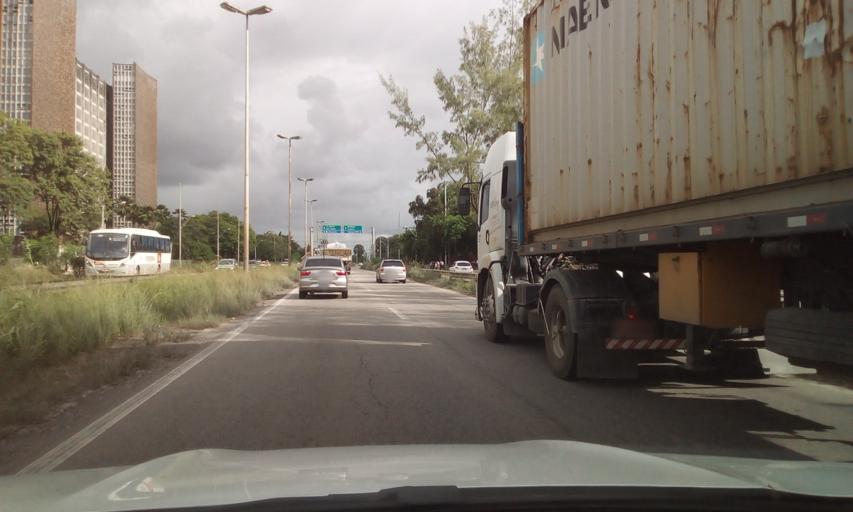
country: BR
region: Pernambuco
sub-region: Recife
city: Recife
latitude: -8.0476
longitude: -34.9453
